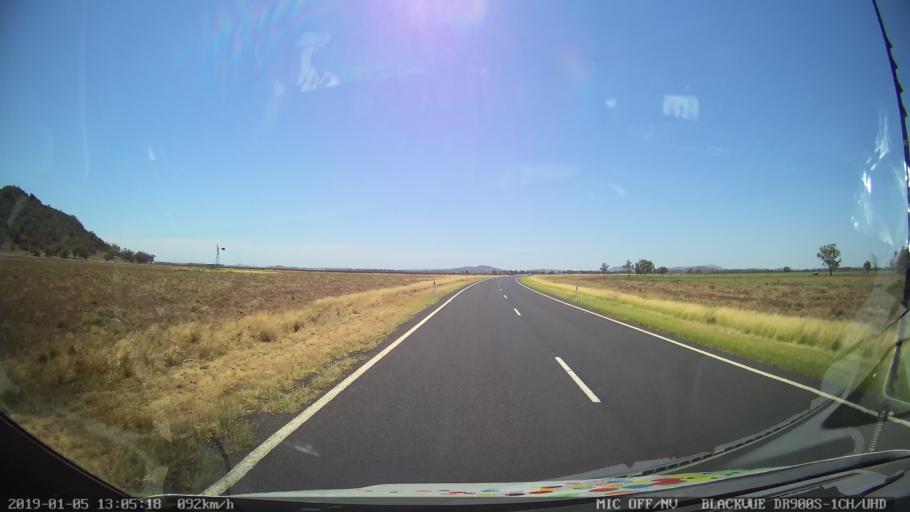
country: AU
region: New South Wales
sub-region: Gunnedah
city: Gunnedah
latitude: -31.0964
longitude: 149.8514
